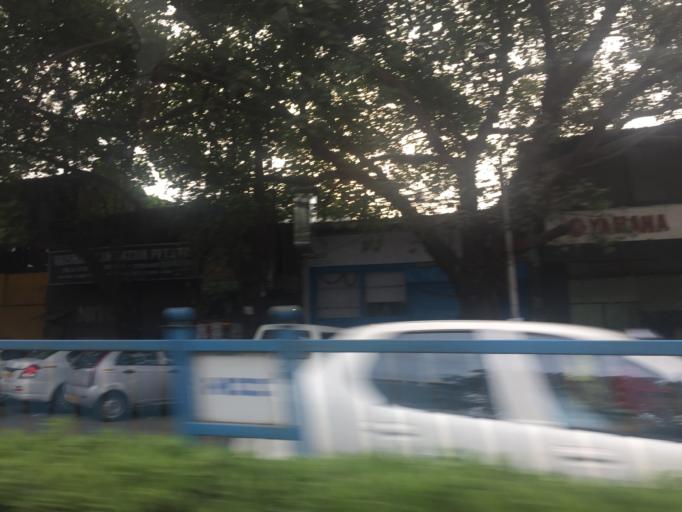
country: IN
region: Maharashtra
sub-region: Mumbai Suburban
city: Powai
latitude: 19.1210
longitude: 72.9256
